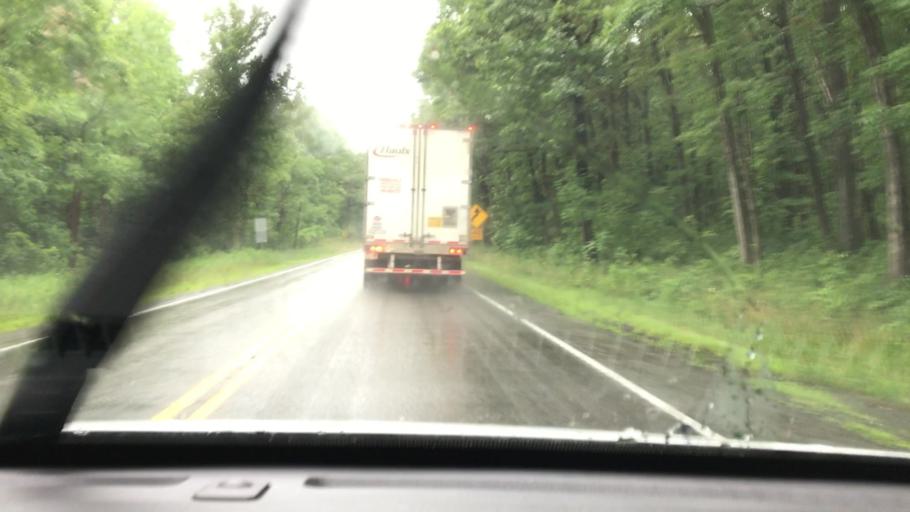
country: US
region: Pennsylvania
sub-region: Clearfield County
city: Osceola Mills
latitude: 40.7808
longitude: -78.2393
